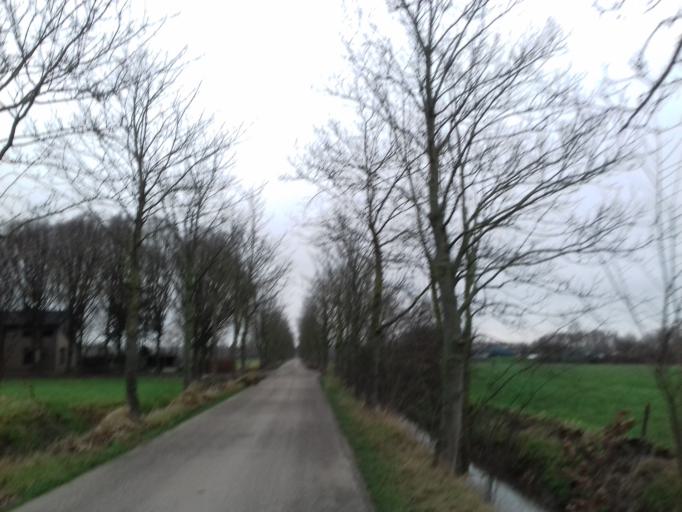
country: NL
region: Gelderland
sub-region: Gemeente Culemborg
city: Culemborg
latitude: 51.9037
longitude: 5.2338
